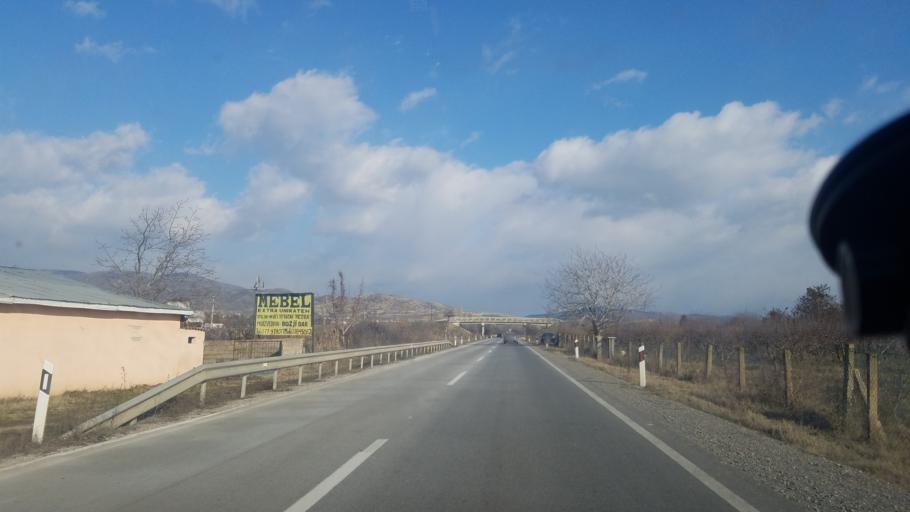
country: MK
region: Kocani
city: Kochani
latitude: 41.9065
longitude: 22.4265
